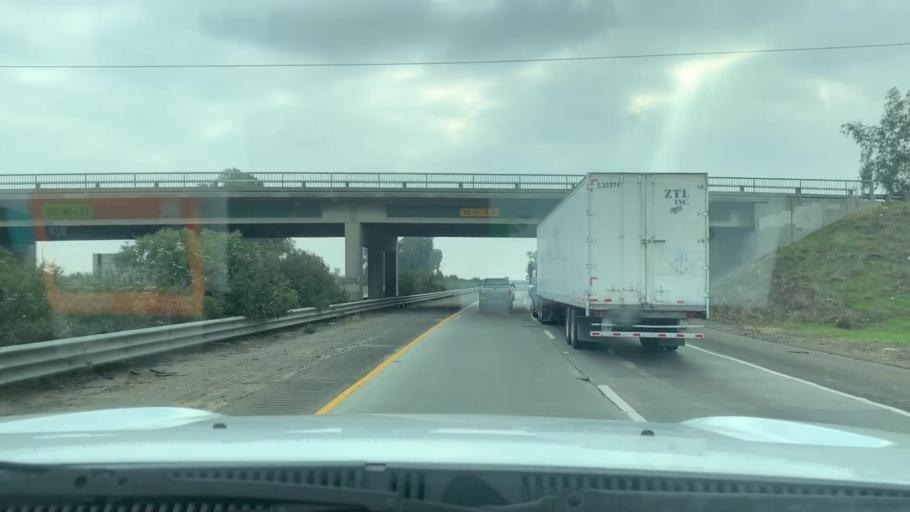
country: US
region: California
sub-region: Tulare County
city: Tipton
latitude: 36.0516
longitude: -119.3111
